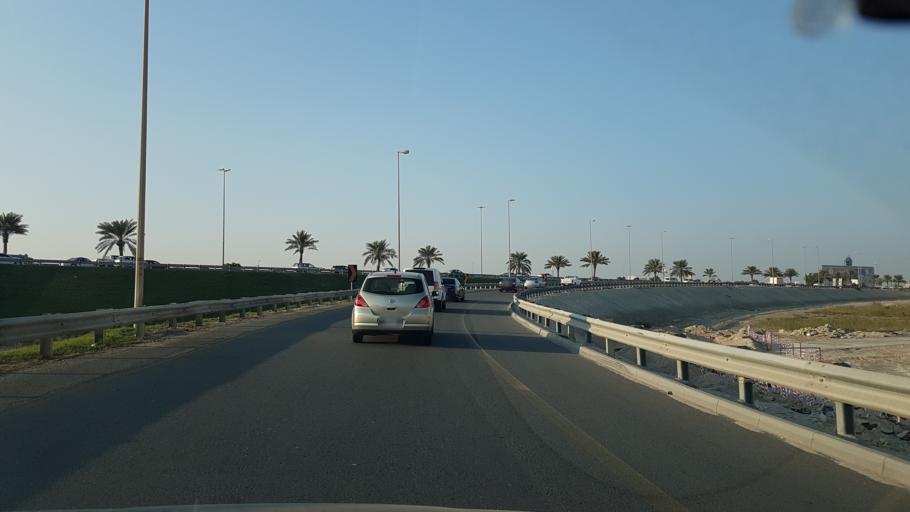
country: BH
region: Northern
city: Madinat `Isa
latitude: 26.1887
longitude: 50.5051
